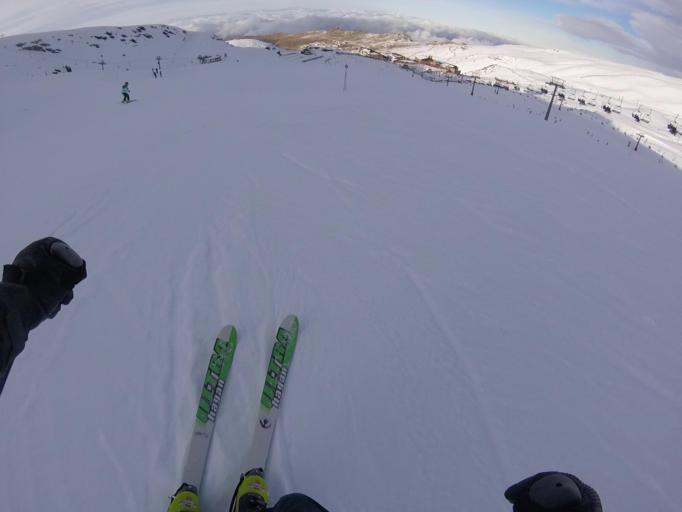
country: ES
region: Andalusia
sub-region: Provincia de Granada
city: Guejar-Sierra
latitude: 37.0664
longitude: -3.3901
